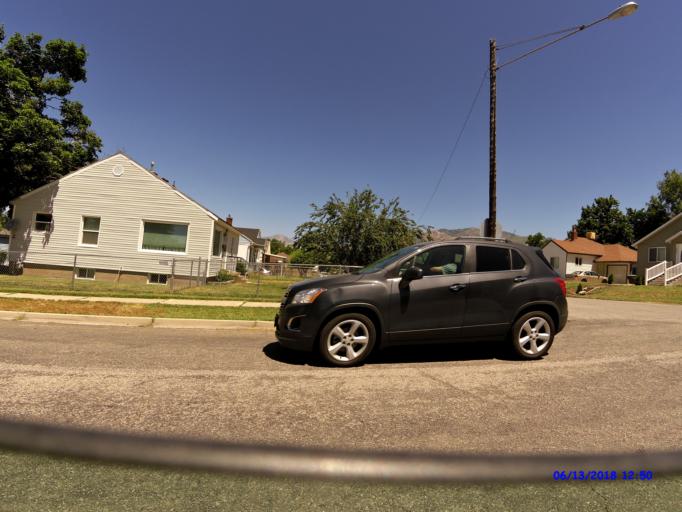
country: US
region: Utah
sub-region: Weber County
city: South Ogden
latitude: 41.2089
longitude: -111.9528
